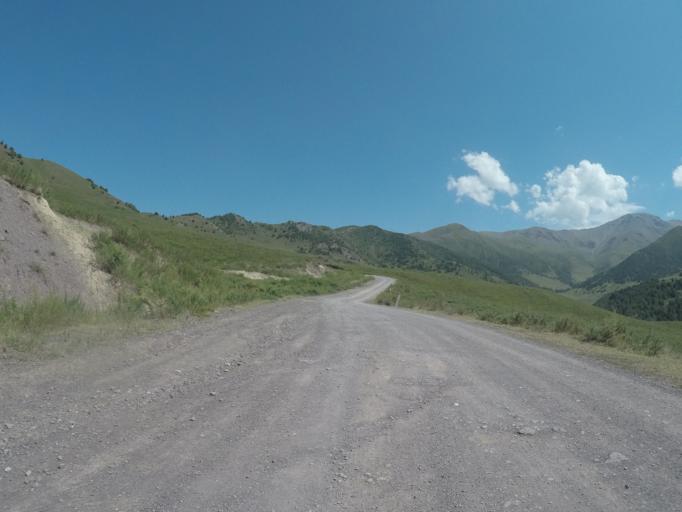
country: KG
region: Chuy
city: Bishkek
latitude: 42.6470
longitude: 74.5231
